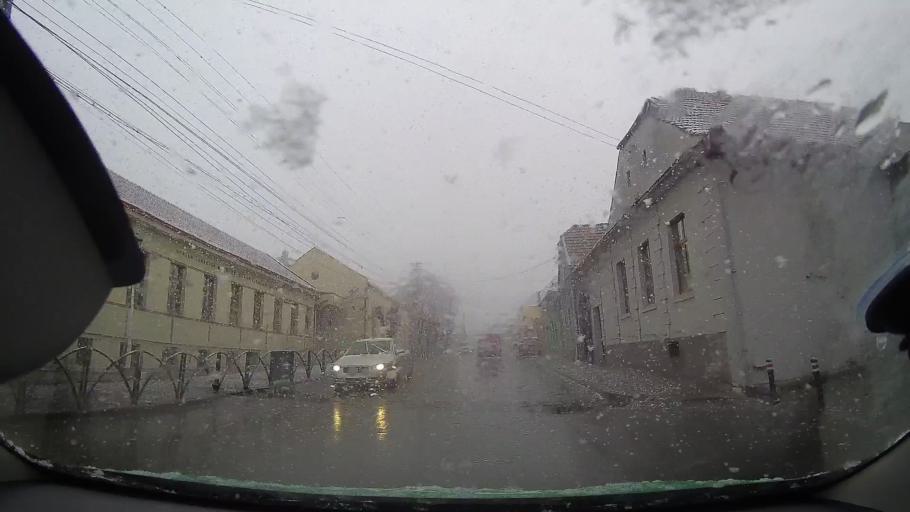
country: RO
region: Sibiu
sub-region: Municipiul Medias
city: Medias
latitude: 46.1692
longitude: 24.3514
